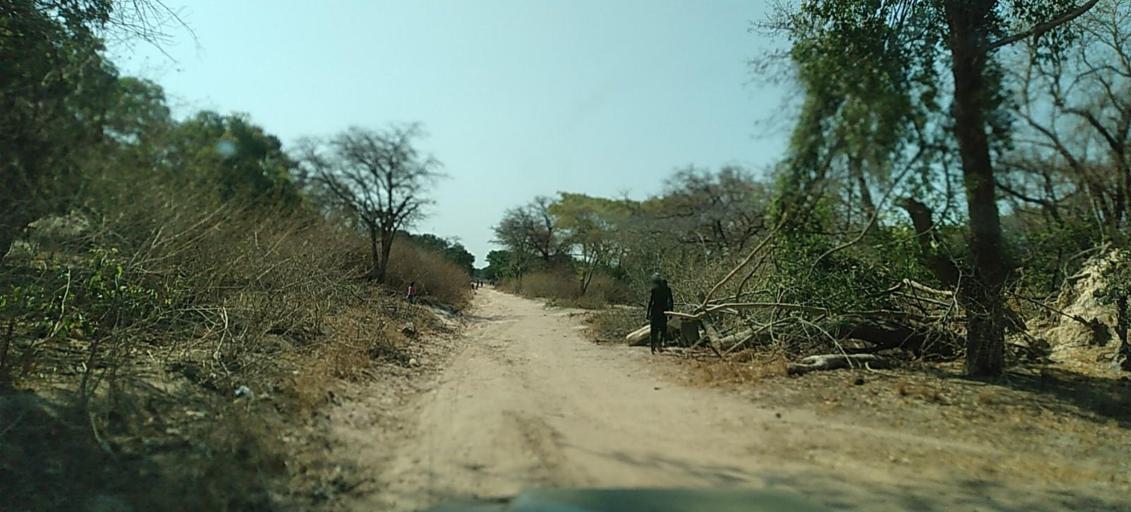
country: ZM
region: North-Western
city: Kalengwa
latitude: -13.3564
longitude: 24.8613
